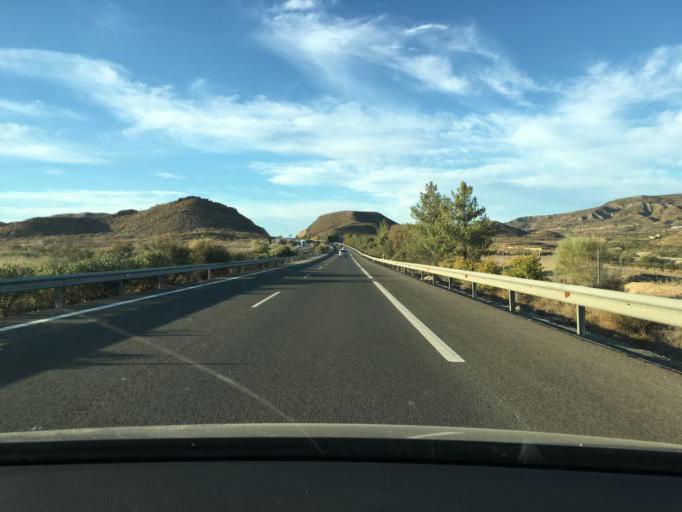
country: ES
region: Andalusia
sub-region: Provincia de Almeria
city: Sorbas
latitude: 37.0538
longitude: -2.0506
